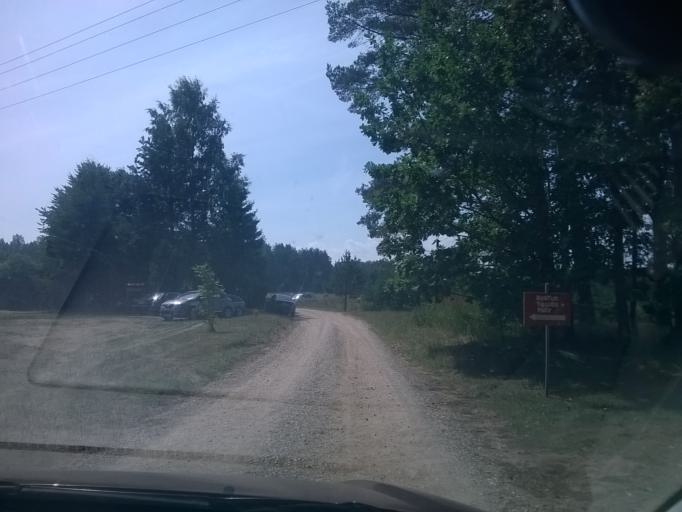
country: EE
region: Tartu
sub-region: Puhja vald
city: Puhja
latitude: 58.2506
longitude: 26.1713
